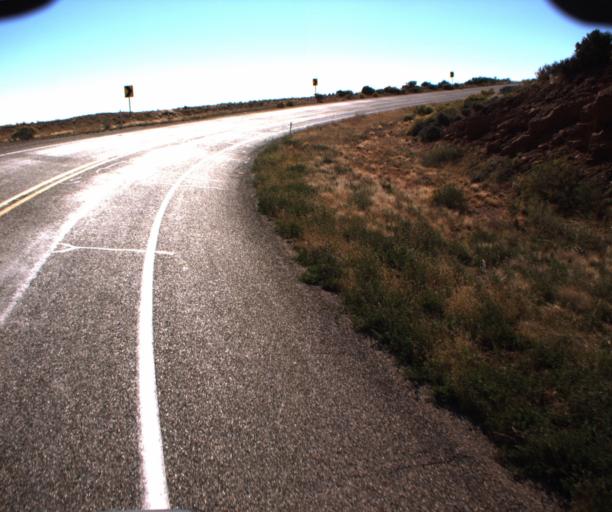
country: US
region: Arizona
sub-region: Coconino County
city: Fredonia
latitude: 36.7266
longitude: -112.0588
